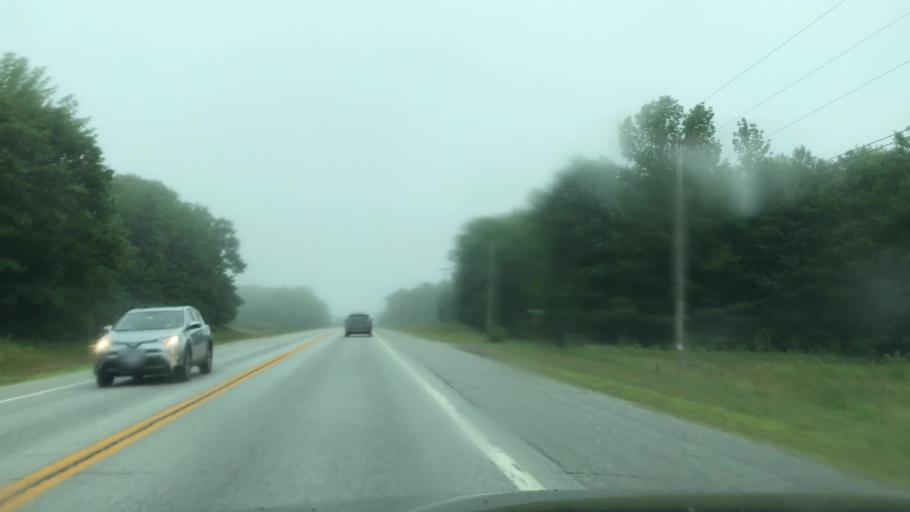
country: US
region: Maine
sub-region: Lincoln County
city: Nobleboro
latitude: 44.0856
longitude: -69.4724
